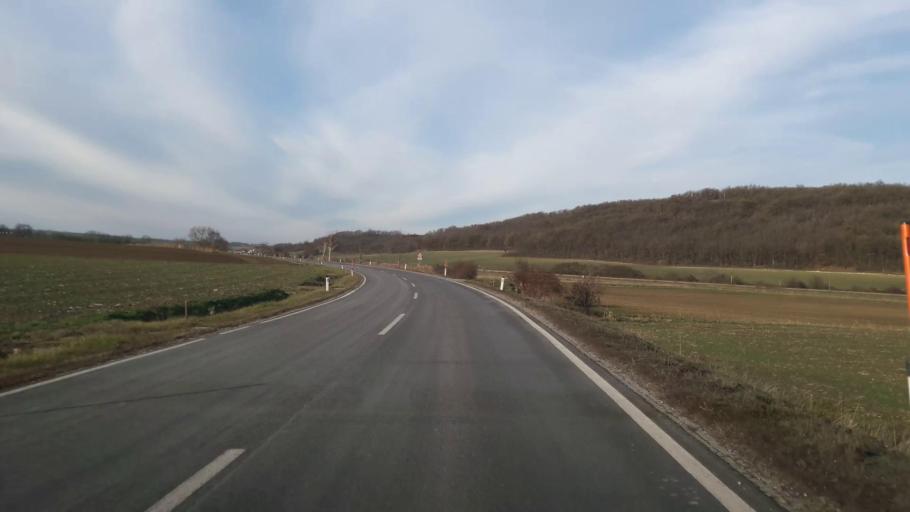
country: AT
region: Lower Austria
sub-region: Politischer Bezirk Ganserndorf
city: Gross-Schweinbarth
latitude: 48.4237
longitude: 16.6252
